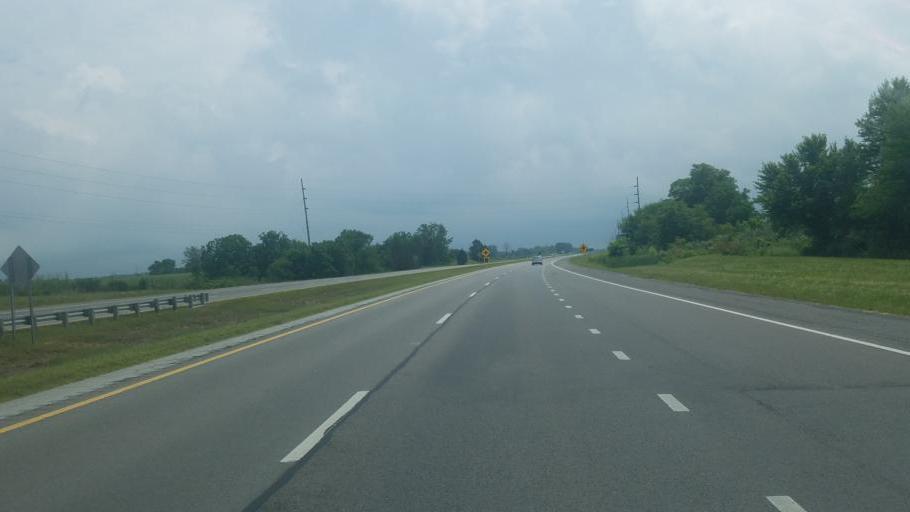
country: US
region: Ohio
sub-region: Logan County
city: Northwood
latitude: 40.4325
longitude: -83.8034
